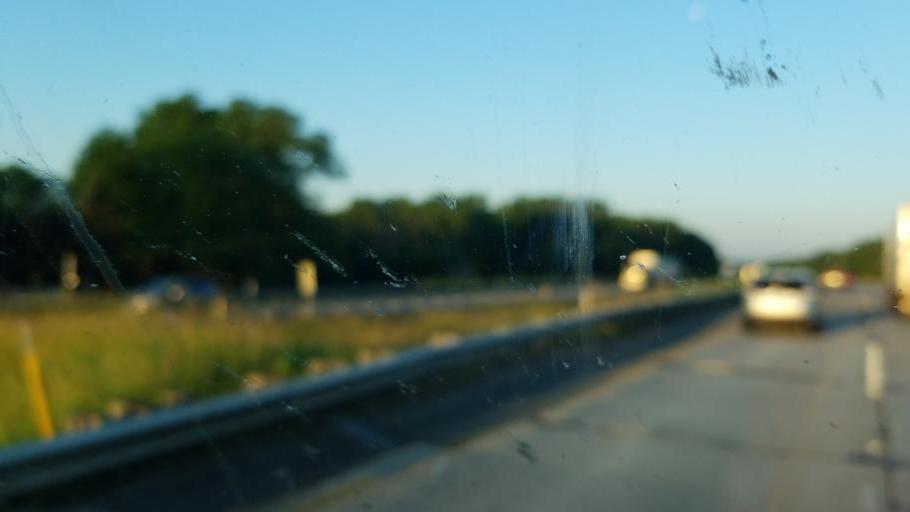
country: US
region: Indiana
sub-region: LaPorte County
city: LaPorte
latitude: 41.6550
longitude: -86.7637
